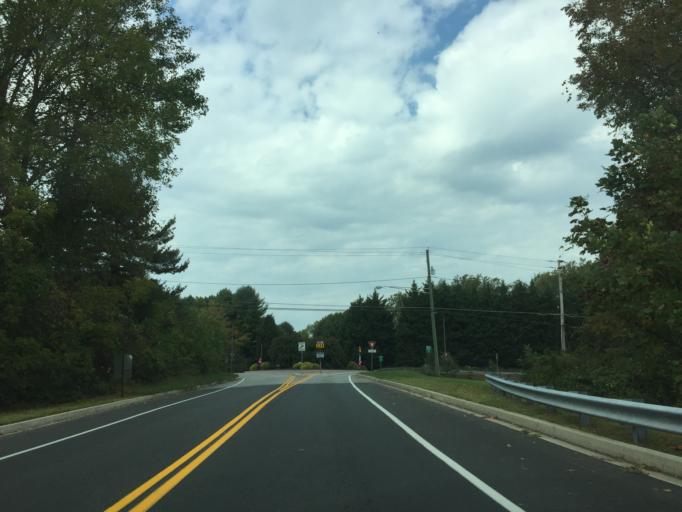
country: US
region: Maryland
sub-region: Harford County
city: Bel Air South
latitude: 39.4936
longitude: -76.3158
